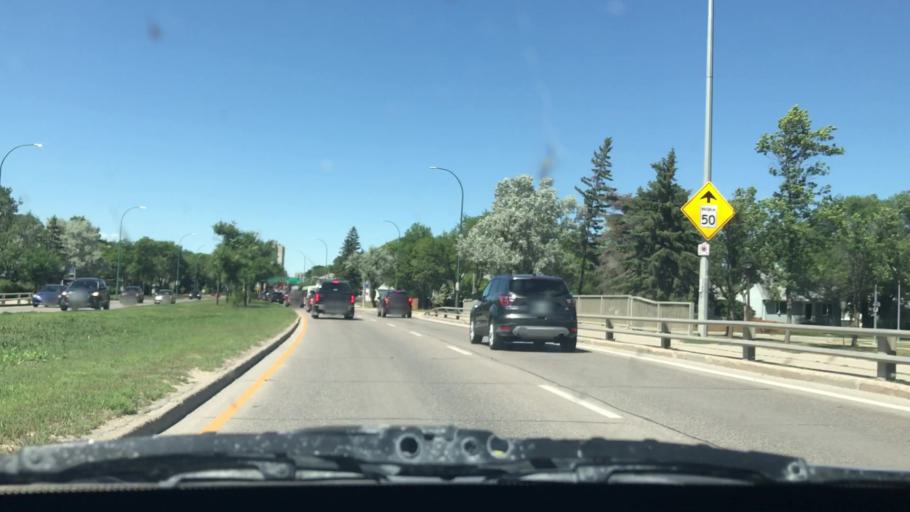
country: CA
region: Manitoba
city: Winnipeg
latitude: 49.8573
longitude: -97.1277
